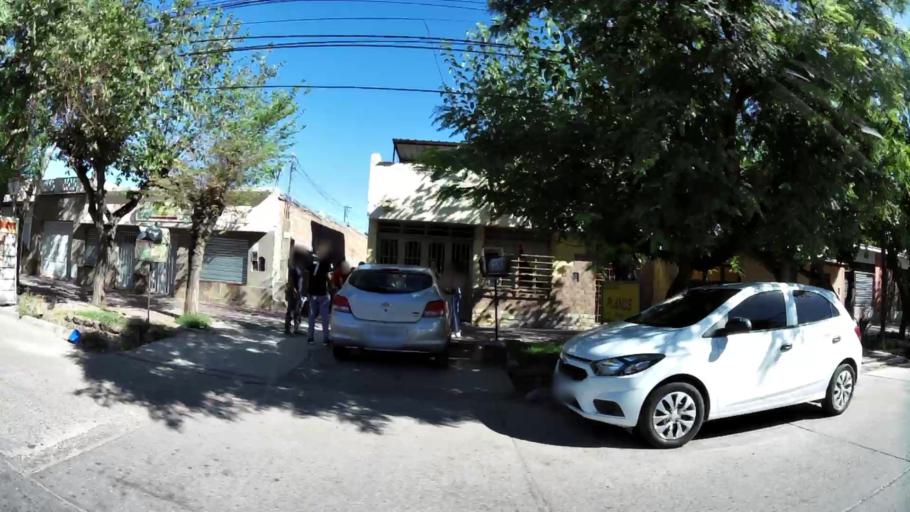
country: AR
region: Mendoza
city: Las Heras
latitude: -32.8425
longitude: -68.8055
